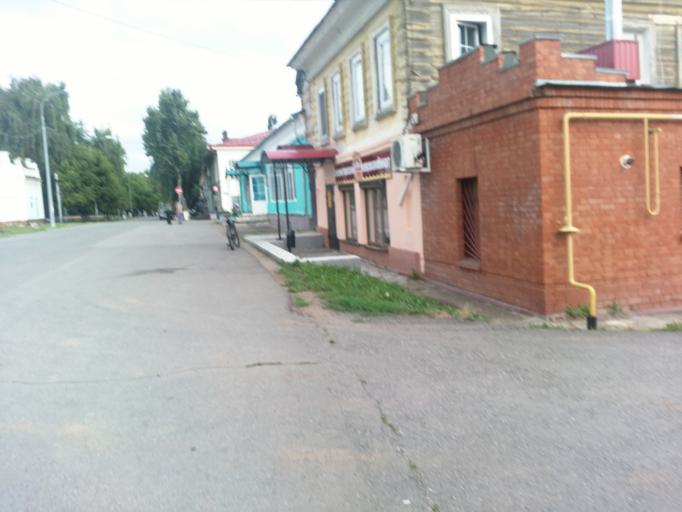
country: RU
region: Tatarstan
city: Yelabuga
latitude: 55.7554
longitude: 52.0638
